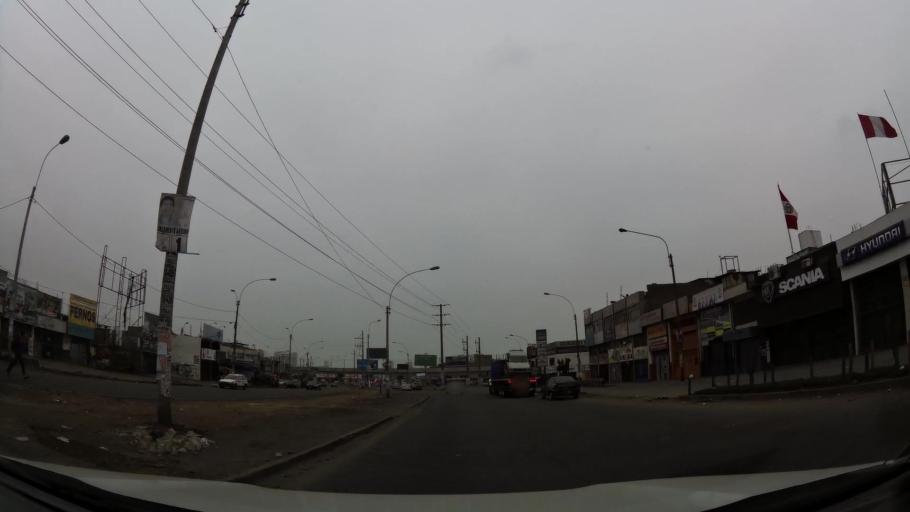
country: PE
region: Lima
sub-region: Lima
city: San Luis
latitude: -12.0758
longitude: -77.0093
